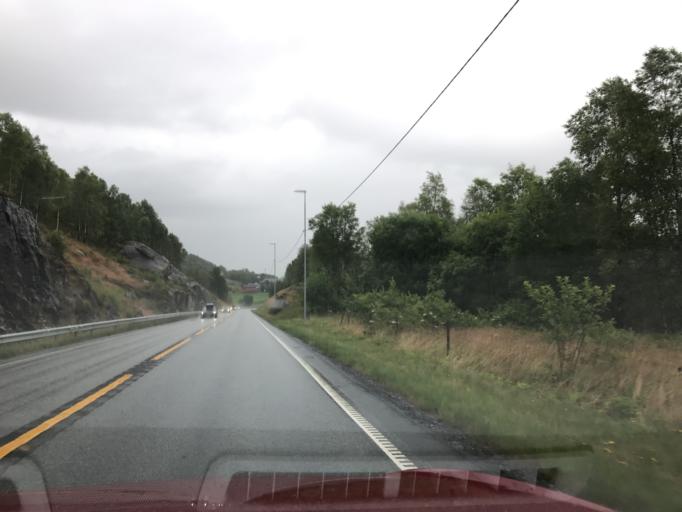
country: NO
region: Rogaland
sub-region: Bjerkreim
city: Vikesa
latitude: 58.5484
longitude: 6.0652
